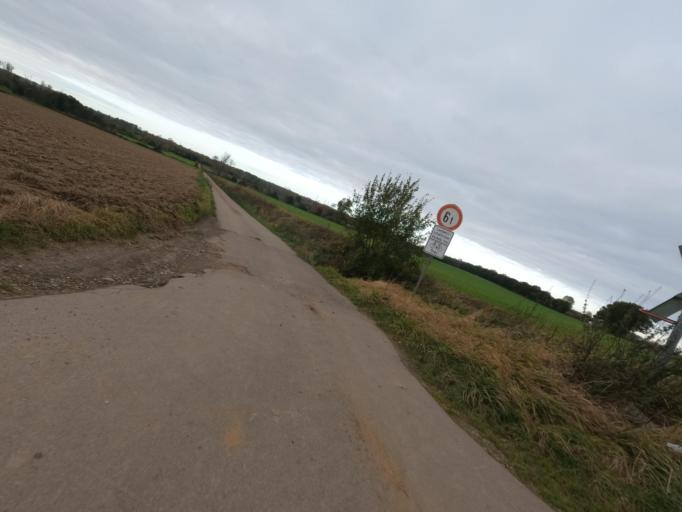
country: DE
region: North Rhine-Westphalia
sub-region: Regierungsbezirk Koln
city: Linnich
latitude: 50.9708
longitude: 6.3127
